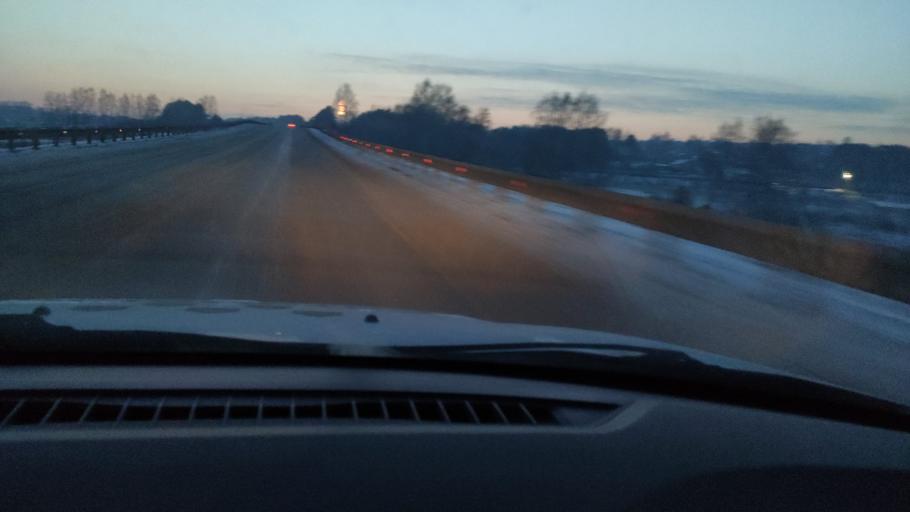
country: RU
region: Perm
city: Kungur
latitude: 57.4232
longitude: 56.9269
